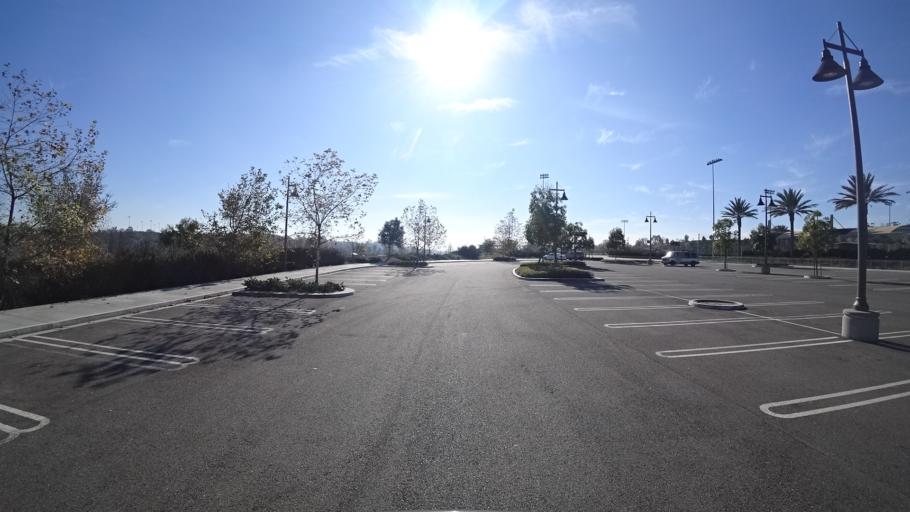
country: US
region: California
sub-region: Orange County
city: Foothill Ranch
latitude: 33.6619
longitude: -117.6559
